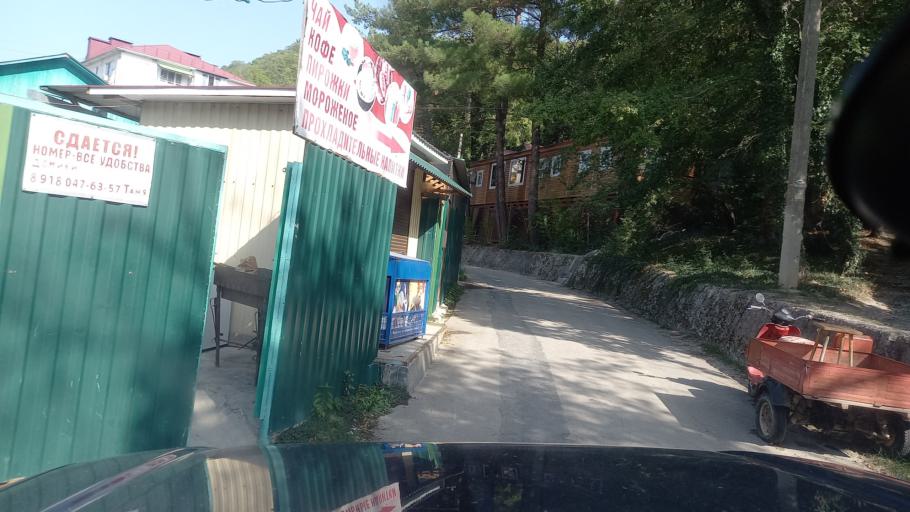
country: RU
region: Krasnodarskiy
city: Pshada
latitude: 44.3760
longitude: 38.4008
